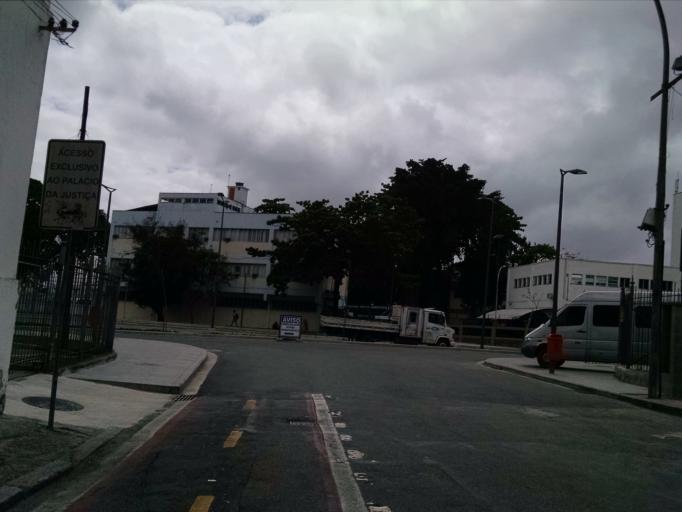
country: BR
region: Rio de Janeiro
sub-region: Rio De Janeiro
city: Rio de Janeiro
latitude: -22.9064
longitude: -43.1690
